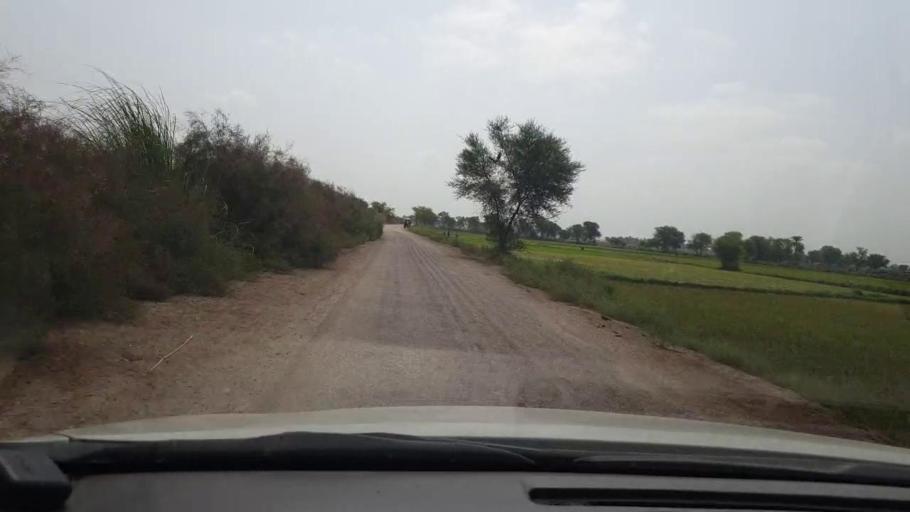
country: PK
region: Sindh
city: Shikarpur
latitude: 28.0074
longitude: 68.5774
